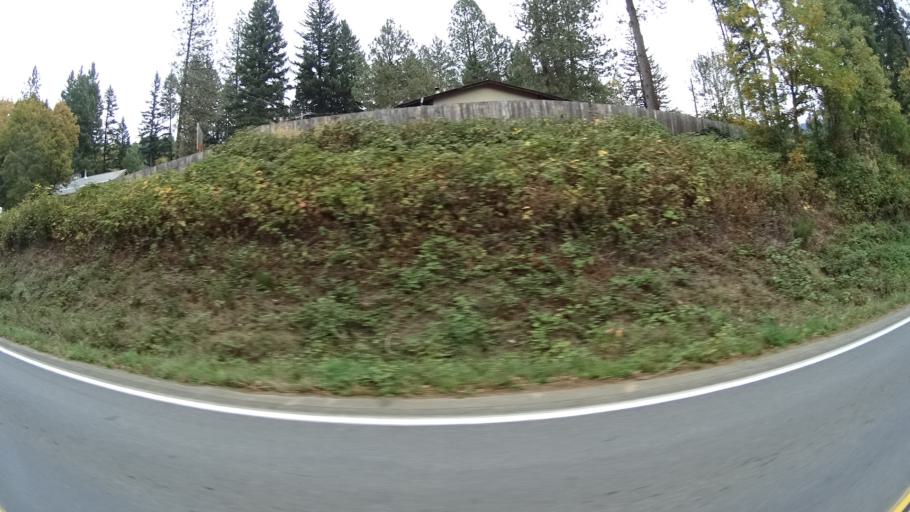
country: US
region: California
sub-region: Siskiyou County
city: Happy Camp
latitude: 41.8023
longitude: -123.3786
